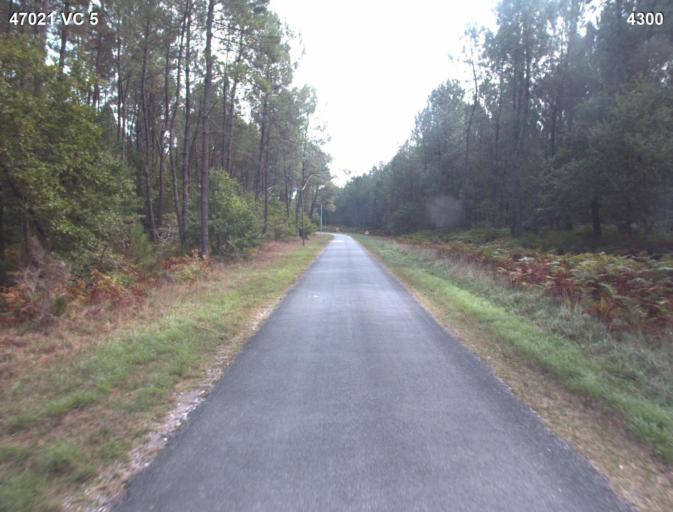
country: FR
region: Aquitaine
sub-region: Departement du Lot-et-Garonne
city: Barbaste
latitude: 44.1444
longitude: 0.2462
